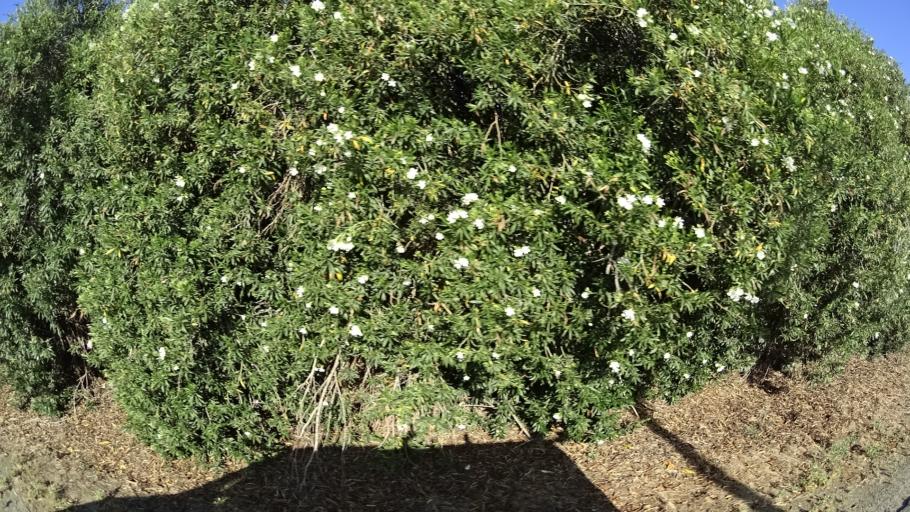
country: US
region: California
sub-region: Kings County
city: Stratford
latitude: 36.1733
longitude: -119.7982
